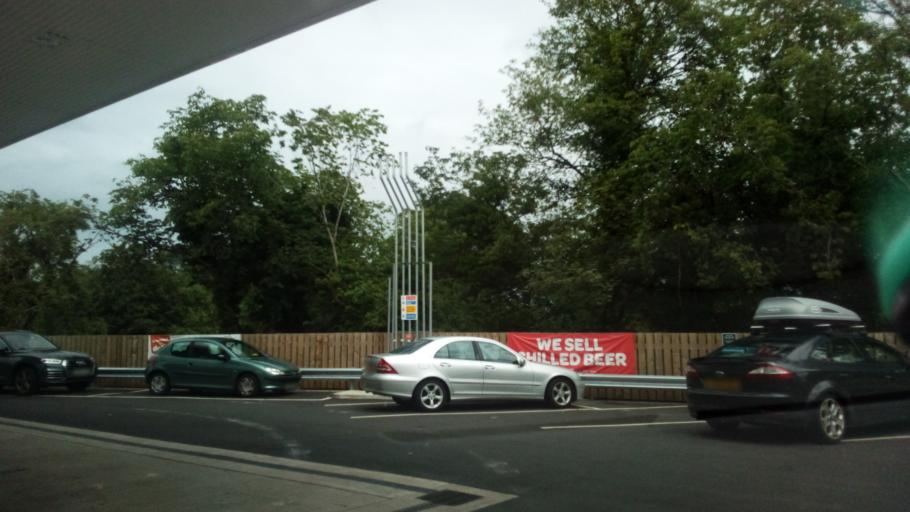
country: GB
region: England
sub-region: Cumbria
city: Kirkby Stephen
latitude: 54.4776
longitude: -2.3499
